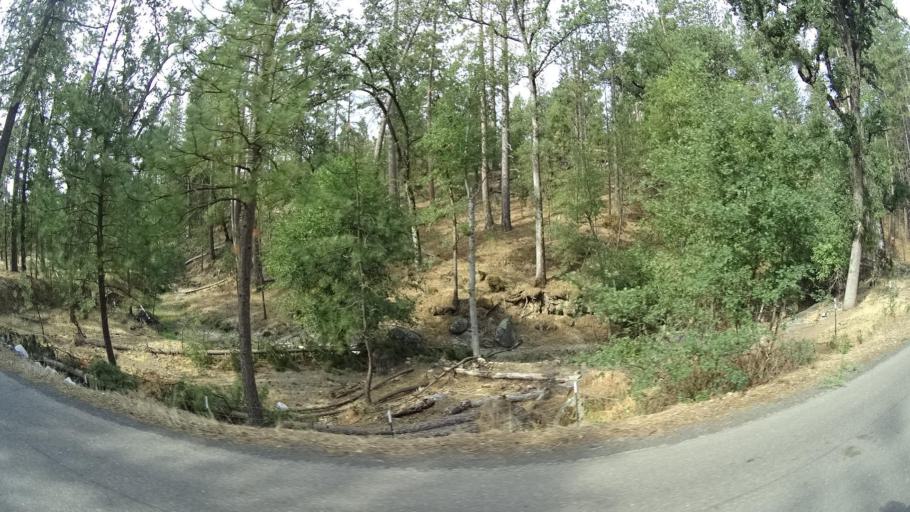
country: US
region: California
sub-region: Madera County
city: Ahwahnee
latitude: 37.4724
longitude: -119.8016
